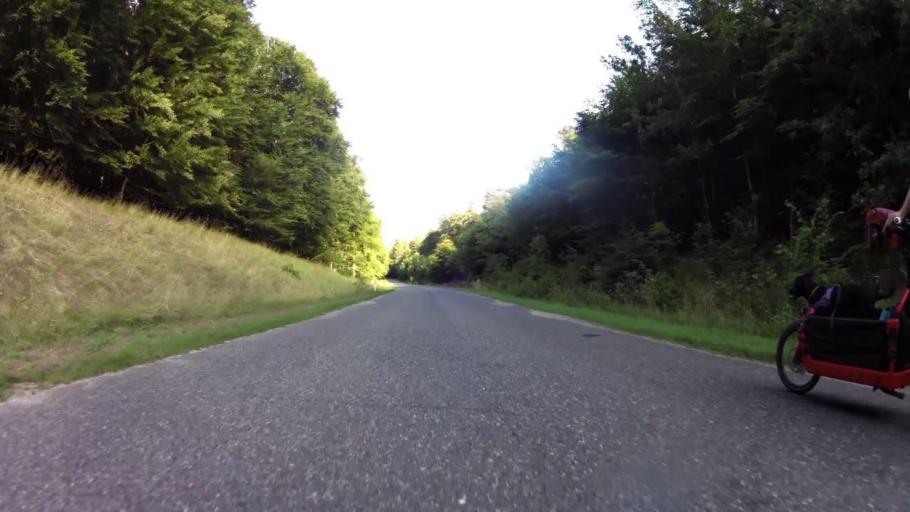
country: PL
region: West Pomeranian Voivodeship
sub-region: Powiat drawski
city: Drawsko Pomorskie
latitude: 53.4708
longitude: 15.8320
